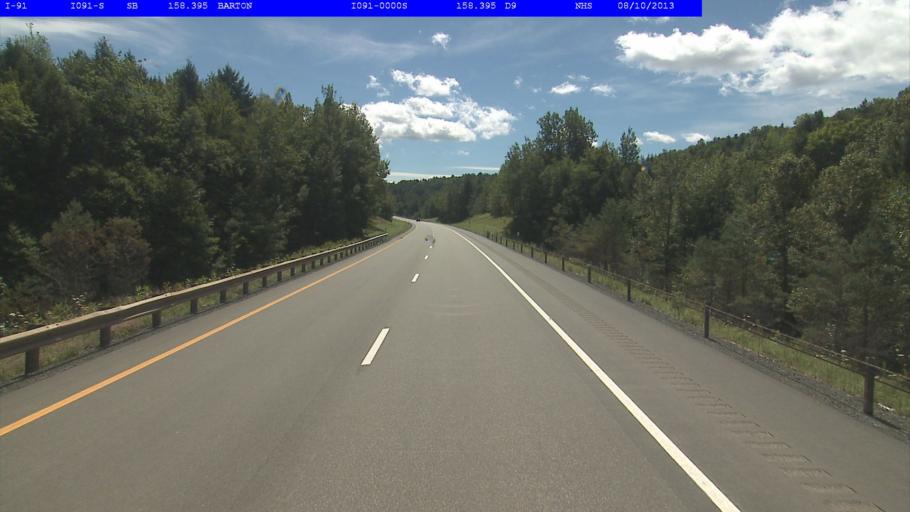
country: US
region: Vermont
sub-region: Orleans County
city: Newport
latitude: 44.7638
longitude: -72.2104
